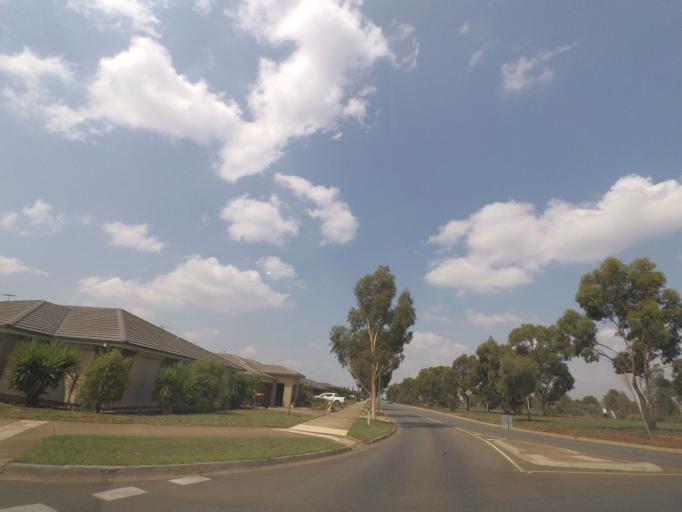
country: AU
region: Victoria
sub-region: Melton
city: Brookfield
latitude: -37.6955
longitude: 144.5477
